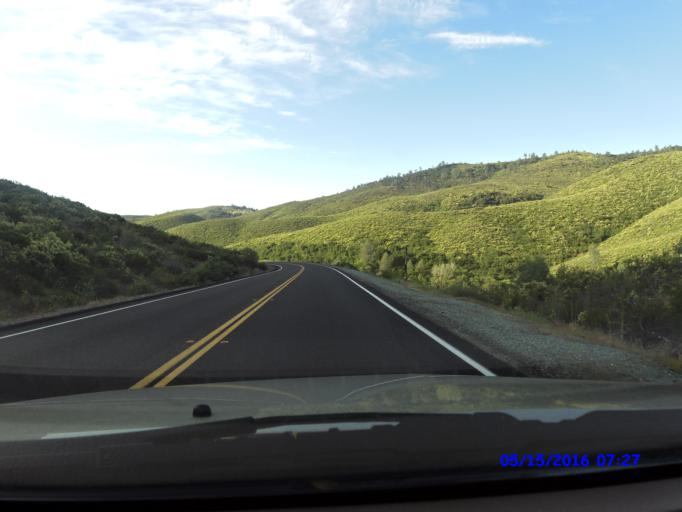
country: US
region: California
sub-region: Tuolumne County
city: Tuolumne City
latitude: 37.7460
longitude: -120.2435
